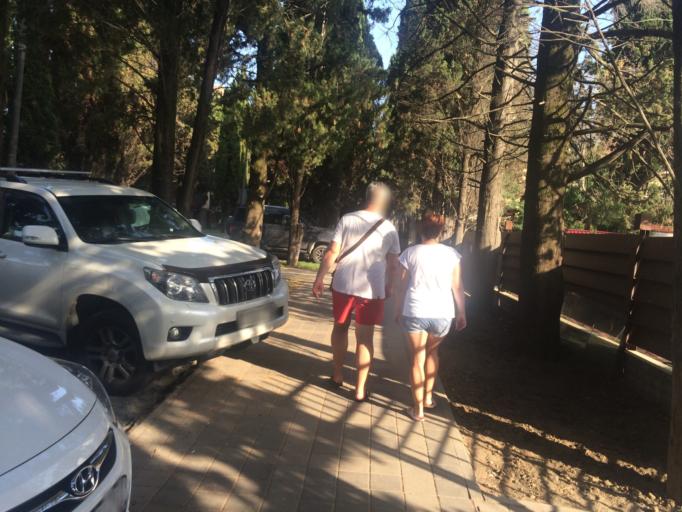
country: RU
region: Krasnodarskiy
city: Adler
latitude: 43.3922
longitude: 39.9817
